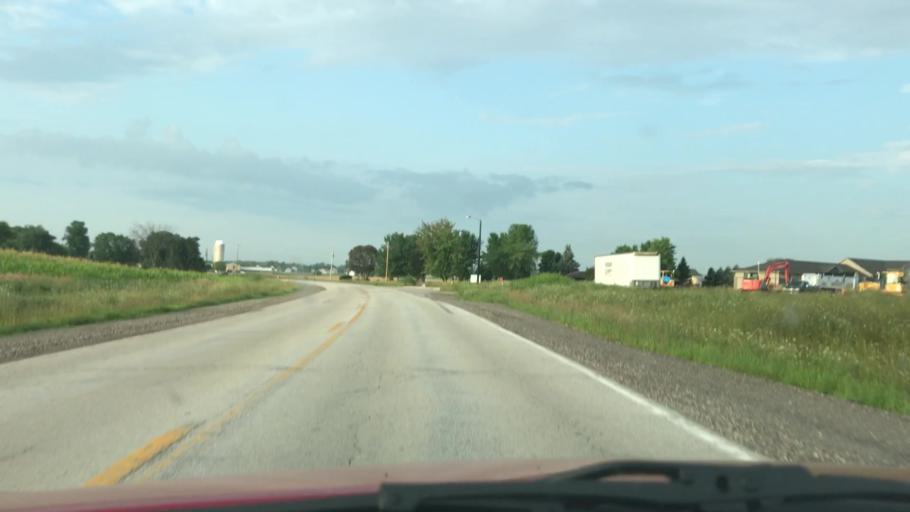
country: US
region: Wisconsin
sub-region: Brown County
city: De Pere
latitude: 44.4402
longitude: -88.1351
